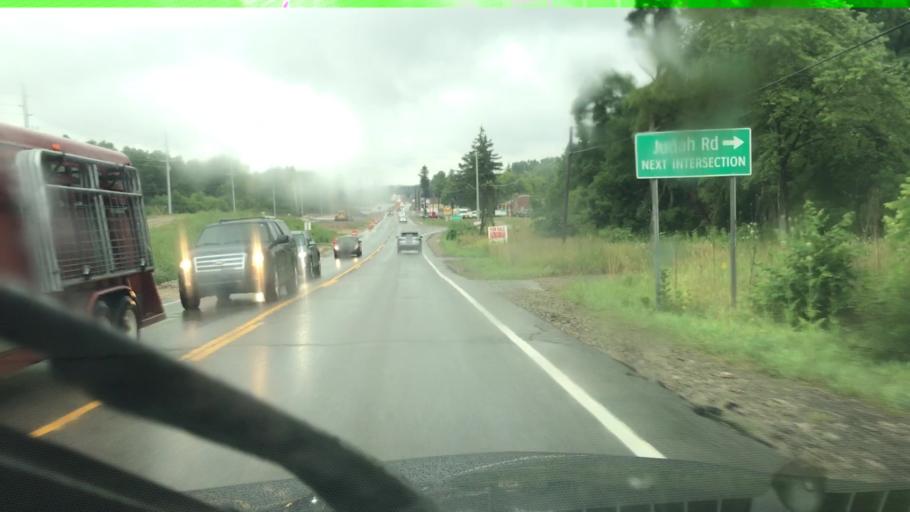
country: US
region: Michigan
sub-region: Oakland County
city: Pontiac
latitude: 42.7138
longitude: -83.3072
